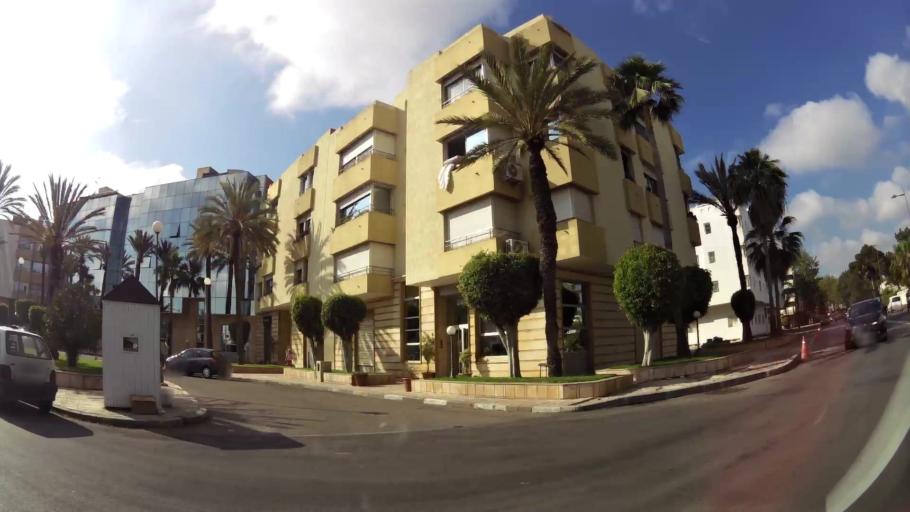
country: MA
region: Rabat-Sale-Zemmour-Zaer
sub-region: Skhirate-Temara
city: Temara
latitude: 33.9605
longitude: -6.8650
